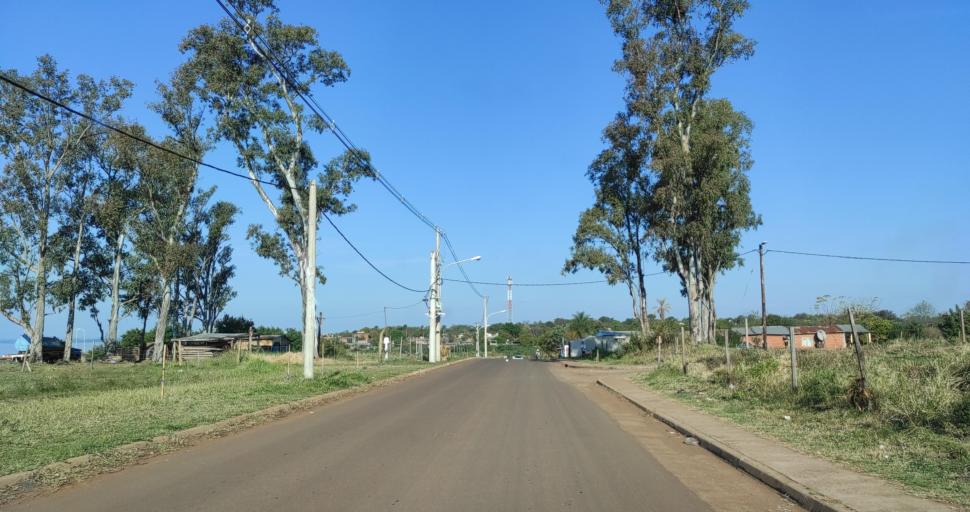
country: AR
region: Misiones
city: Garupa
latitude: -27.4343
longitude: -55.8643
